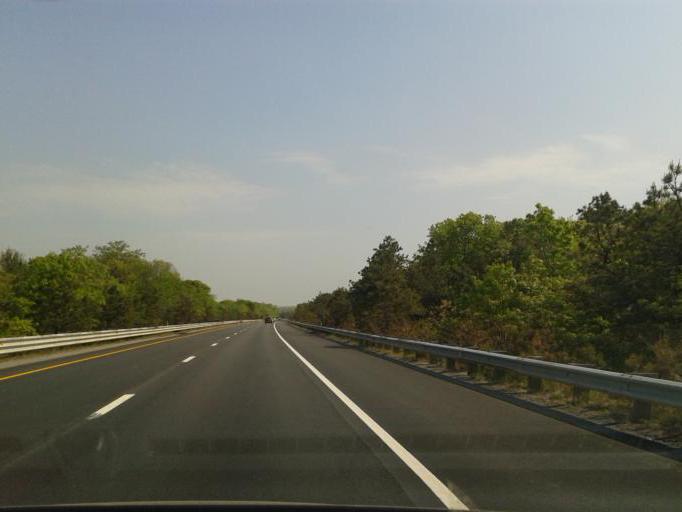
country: US
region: Massachusetts
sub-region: Barnstable County
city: Pocasset
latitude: 41.6767
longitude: -70.5957
